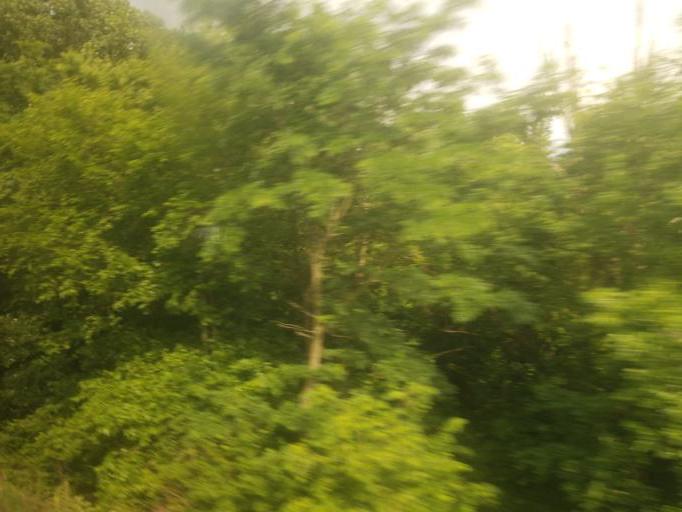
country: US
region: Illinois
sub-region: Bureau County
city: Princeton
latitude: 41.3586
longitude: -89.5988
